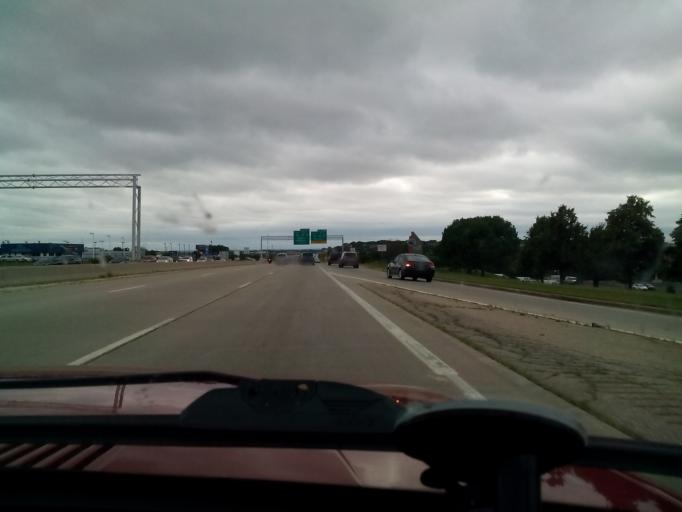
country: US
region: Wisconsin
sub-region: Dane County
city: Sun Prairie
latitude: 43.1442
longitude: -89.2877
